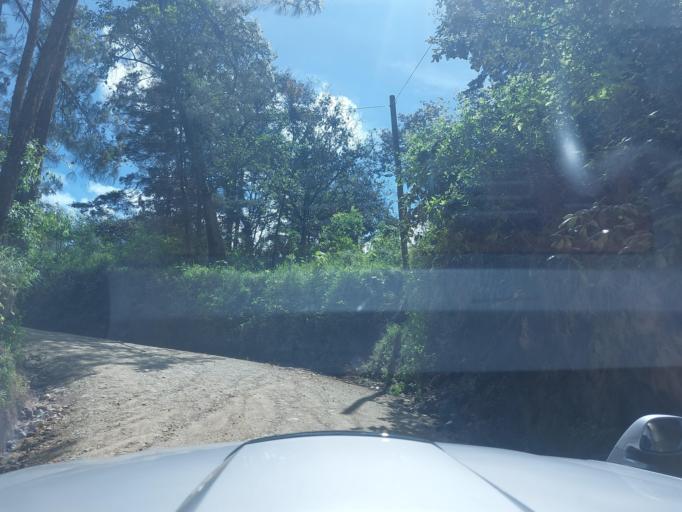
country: GT
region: Chimaltenango
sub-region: Municipio de San Juan Comalapa
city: Comalapa
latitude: 14.7554
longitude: -90.8888
